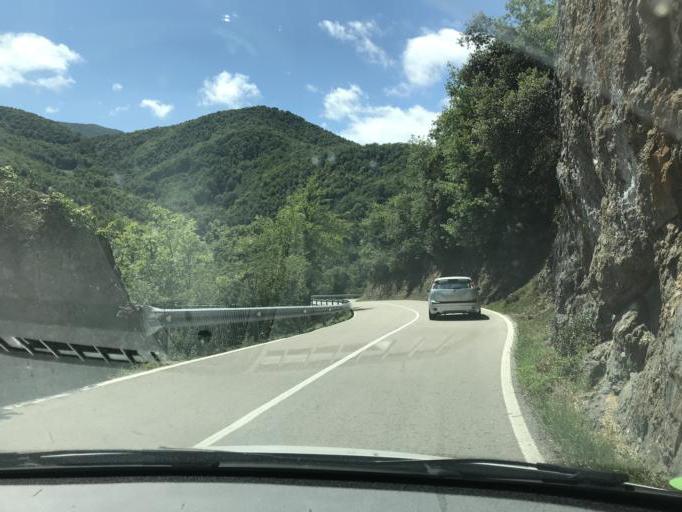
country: ES
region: Cantabria
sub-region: Provincia de Cantabria
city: Cabezon de Liebana
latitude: 43.0768
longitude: -4.5065
